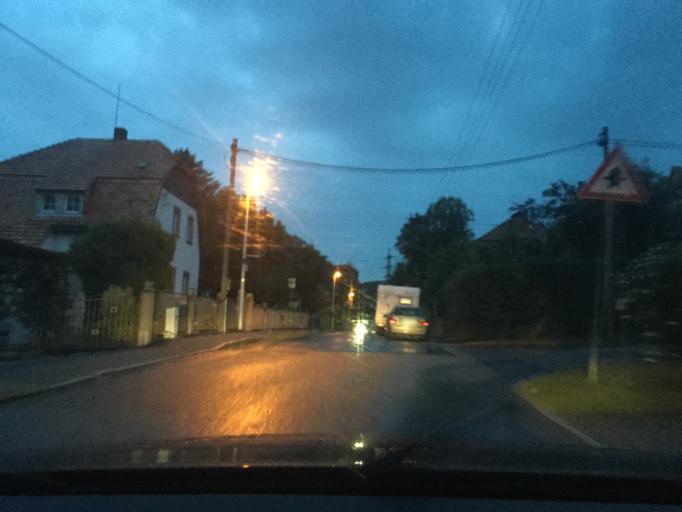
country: DE
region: Saxony
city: Coswig
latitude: 51.0916
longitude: 13.6031
